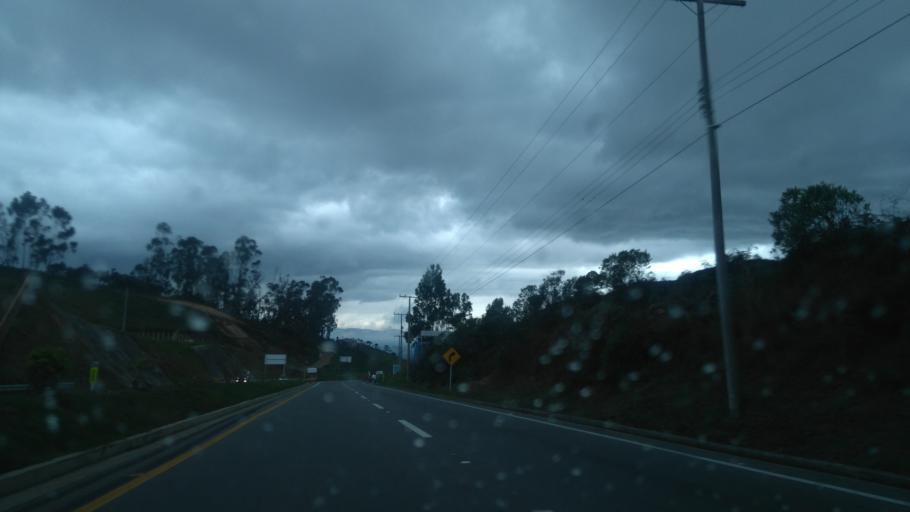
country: CO
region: Cundinamarca
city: El Rosal
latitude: 4.8632
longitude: -74.2900
